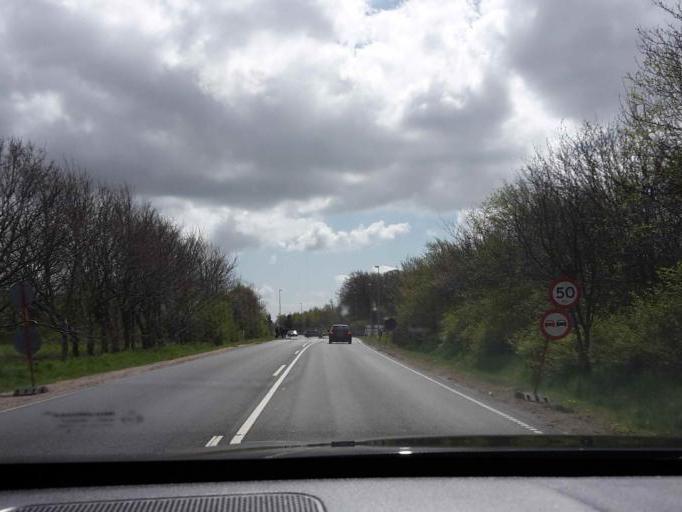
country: DK
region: South Denmark
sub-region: Esbjerg Kommune
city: Tjaereborg
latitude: 55.5260
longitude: 8.5856
